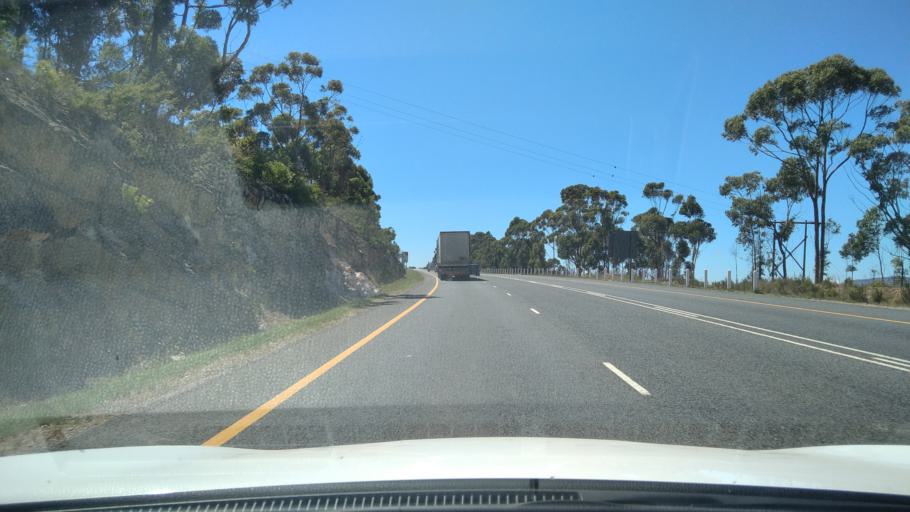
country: ZA
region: Western Cape
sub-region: Overberg District Municipality
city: Caledon
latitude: -34.2217
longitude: 19.4075
